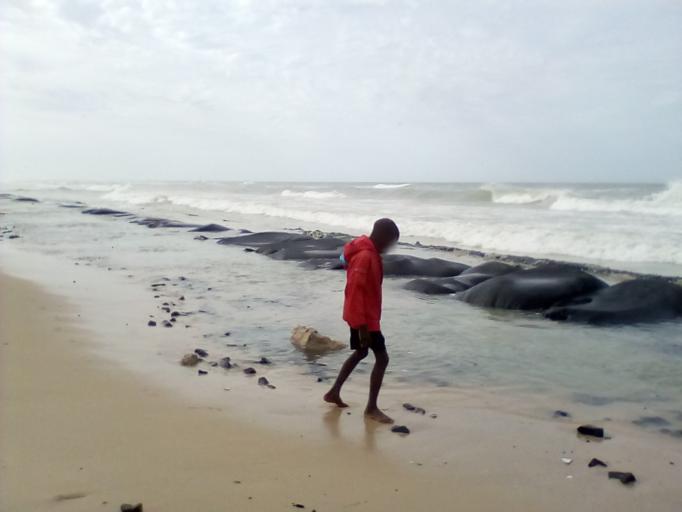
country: SN
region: Saint-Louis
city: Saint-Louis
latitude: 16.0440
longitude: -16.5088
